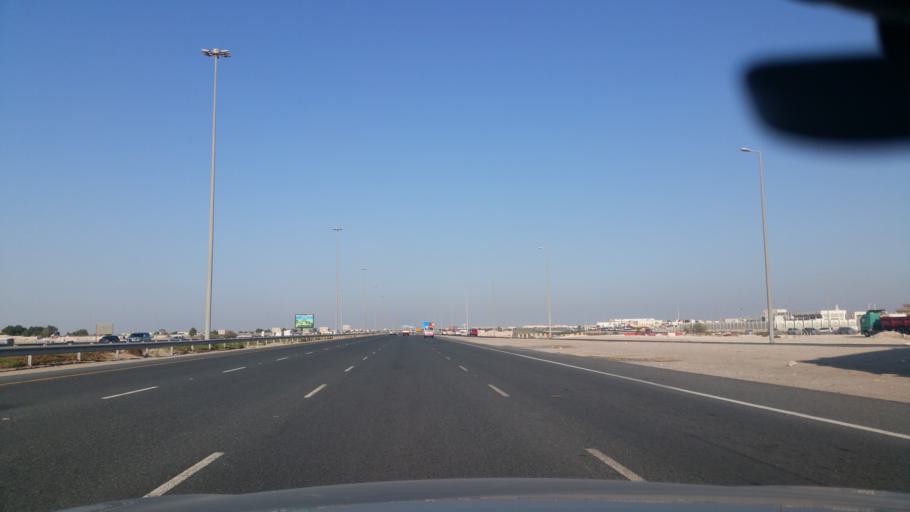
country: QA
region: Baladiyat ar Rayyan
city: Ar Rayyan
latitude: 25.1890
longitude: 51.3693
